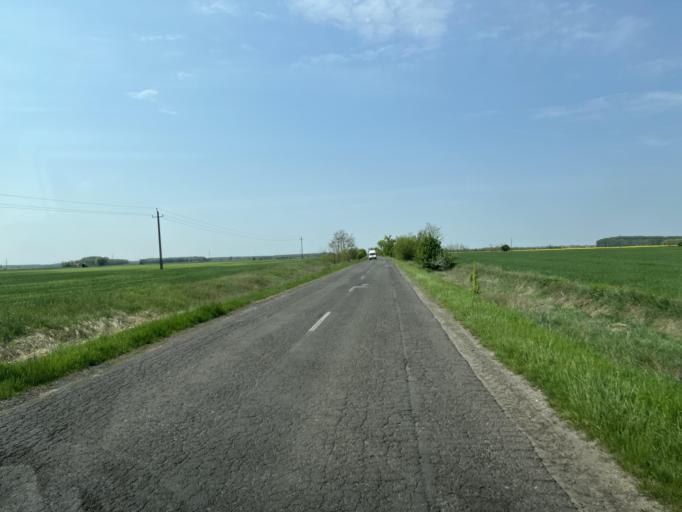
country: HU
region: Pest
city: Nagykoros
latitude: 47.0446
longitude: 19.8337
